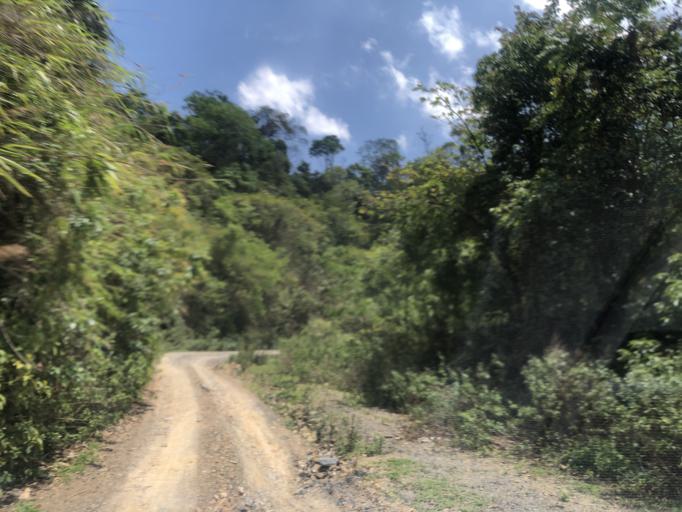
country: LA
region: Phongsali
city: Phongsali
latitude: 21.4430
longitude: 102.1632
